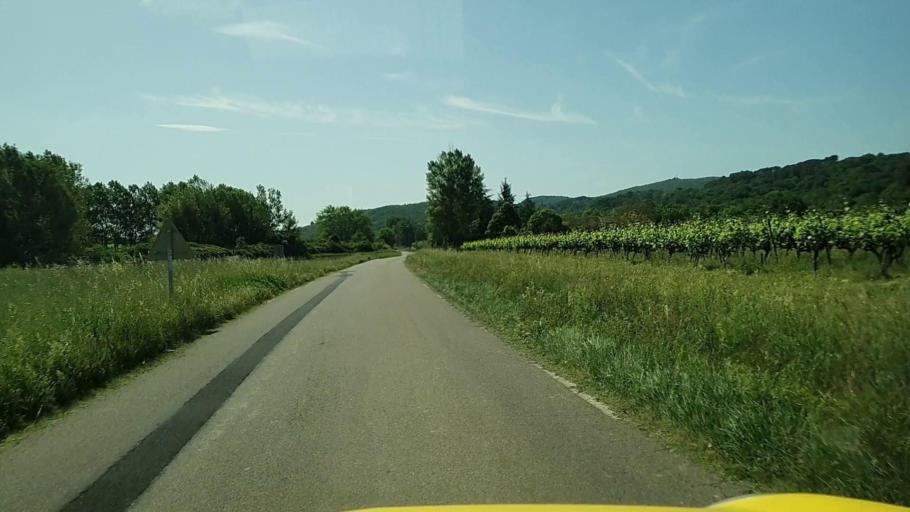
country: FR
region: Languedoc-Roussillon
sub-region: Departement du Gard
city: Tresques
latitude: 44.1035
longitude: 4.5432
